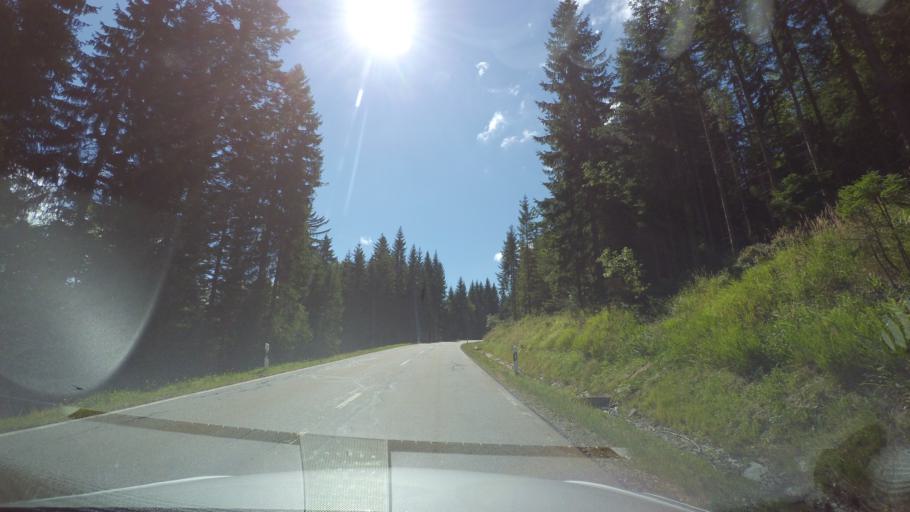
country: DE
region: Bavaria
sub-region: Lower Bavaria
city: Bayerisch Eisenstein
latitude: 49.0899
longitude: 13.1654
